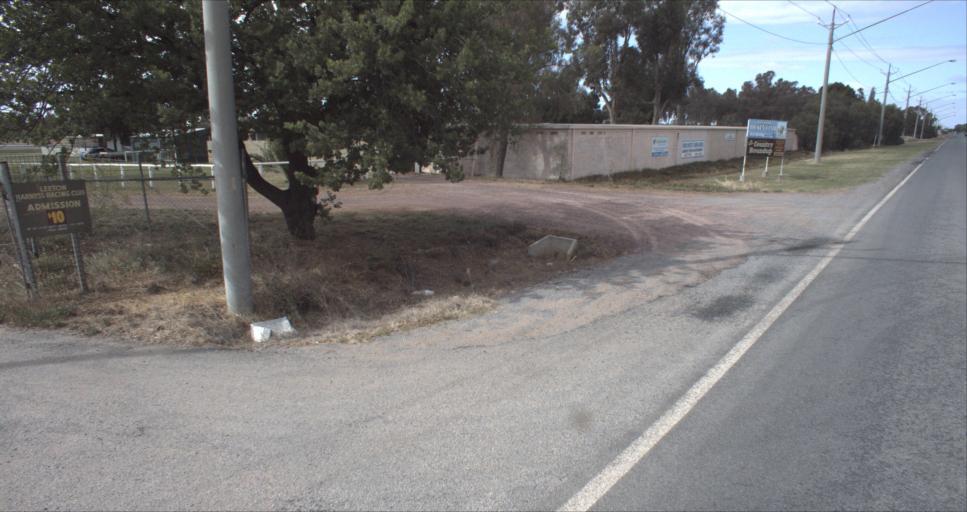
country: AU
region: New South Wales
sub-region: Leeton
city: Leeton
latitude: -34.5611
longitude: 146.4014
